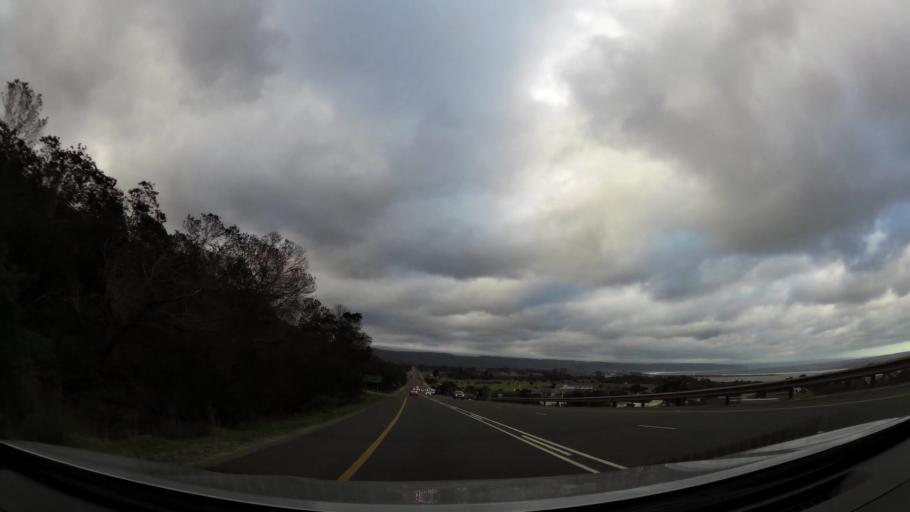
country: ZA
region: Western Cape
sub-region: Eden District Municipality
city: Plettenberg Bay
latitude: -34.0428
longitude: 23.3683
